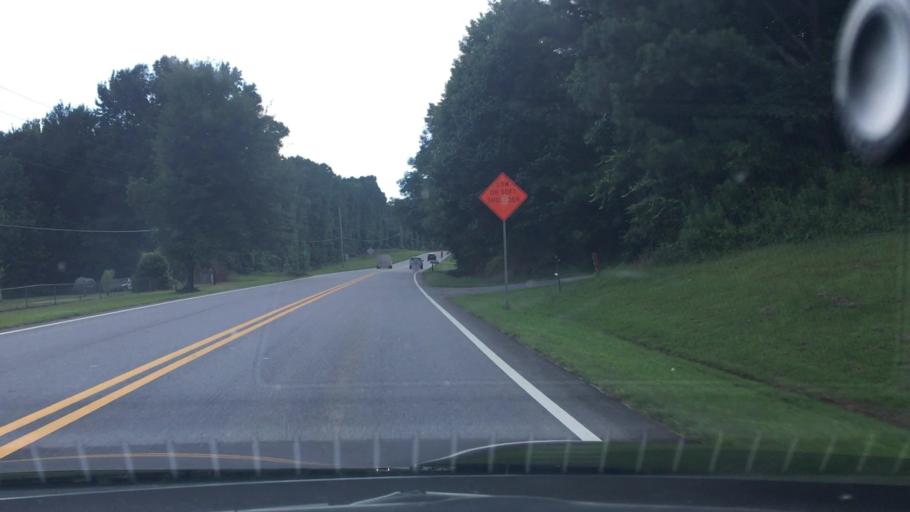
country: US
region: Georgia
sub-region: Butts County
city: Jackson
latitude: 33.2882
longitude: -84.0232
